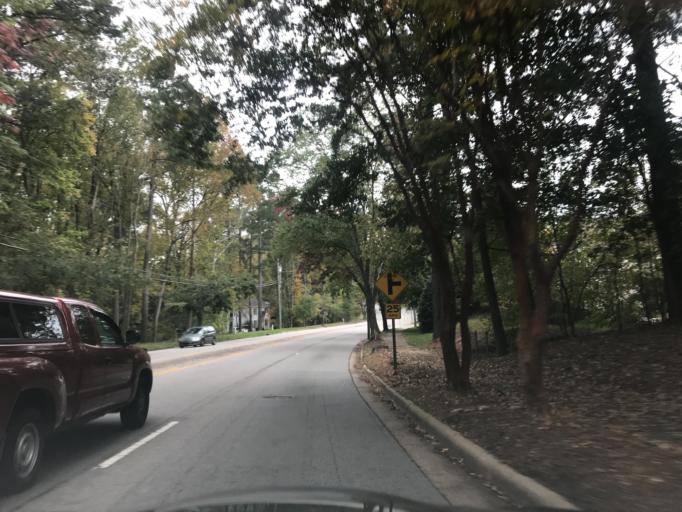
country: US
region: North Carolina
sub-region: Wake County
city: West Raleigh
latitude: 35.8510
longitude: -78.6211
